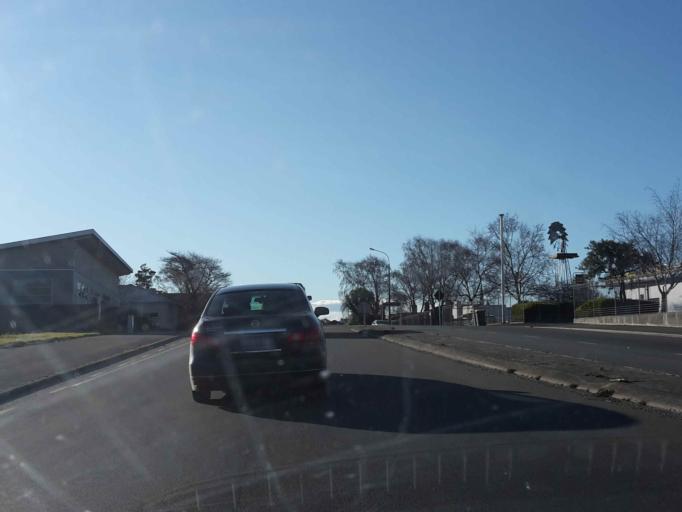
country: NZ
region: Canterbury
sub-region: Timaru District
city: Timaru
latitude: -44.4004
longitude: 171.2485
